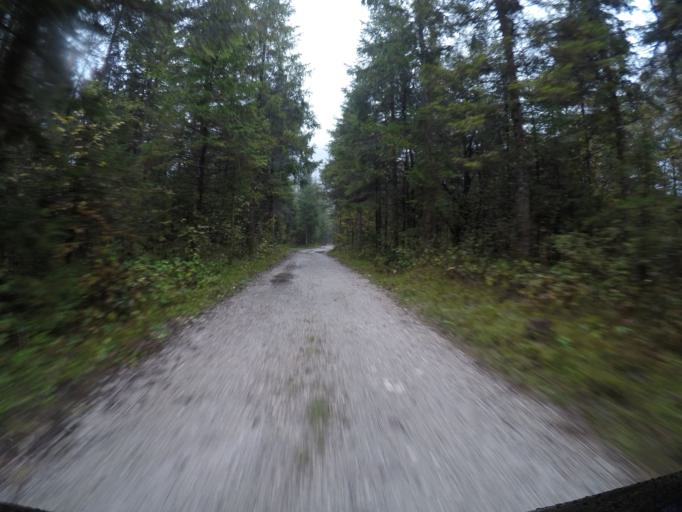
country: SI
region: Bovec
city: Bovec
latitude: 46.3329
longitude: 13.6376
